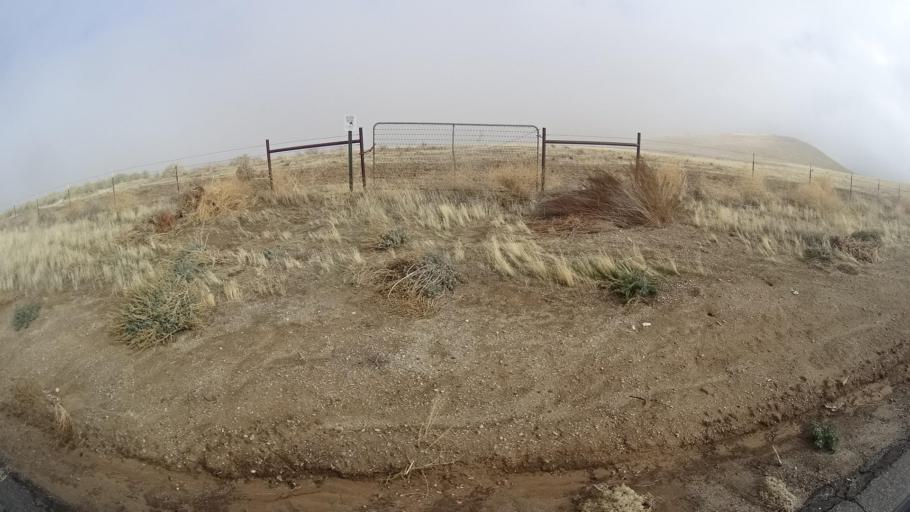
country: US
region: California
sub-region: Kern County
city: Maricopa
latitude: 34.9317
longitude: -119.4130
